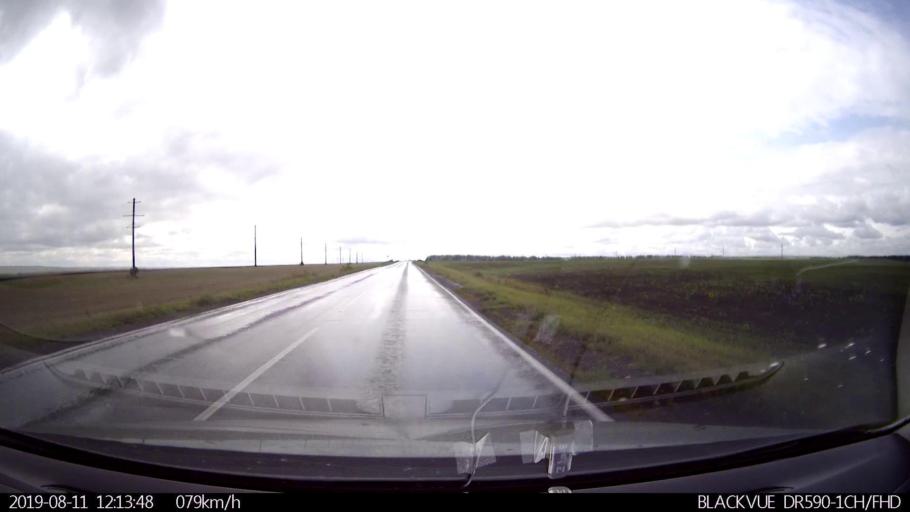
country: RU
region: Ulyanovsk
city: Ignatovka
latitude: 53.9583
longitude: 47.9884
